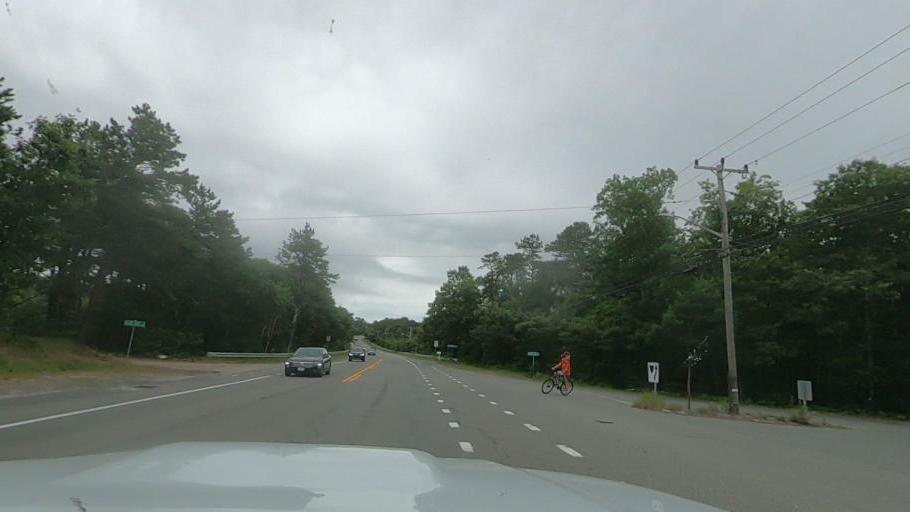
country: US
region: Massachusetts
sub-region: Barnstable County
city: Wellfleet
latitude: 41.9611
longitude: -70.0293
